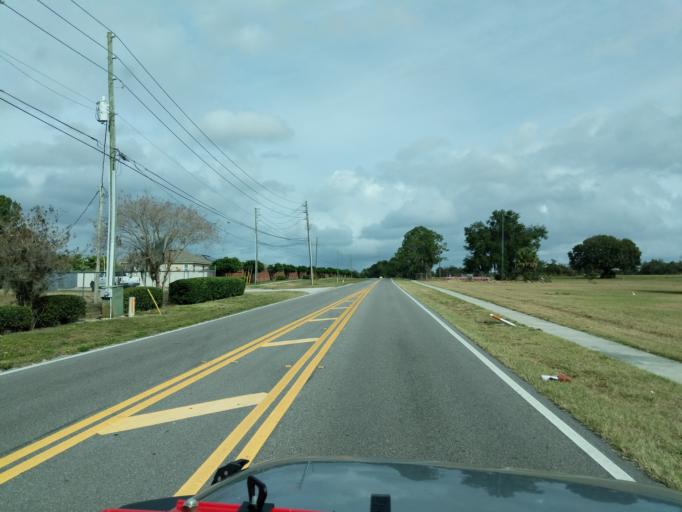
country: US
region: Florida
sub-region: Orange County
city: Paradise Heights
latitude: 28.6074
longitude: -81.5495
